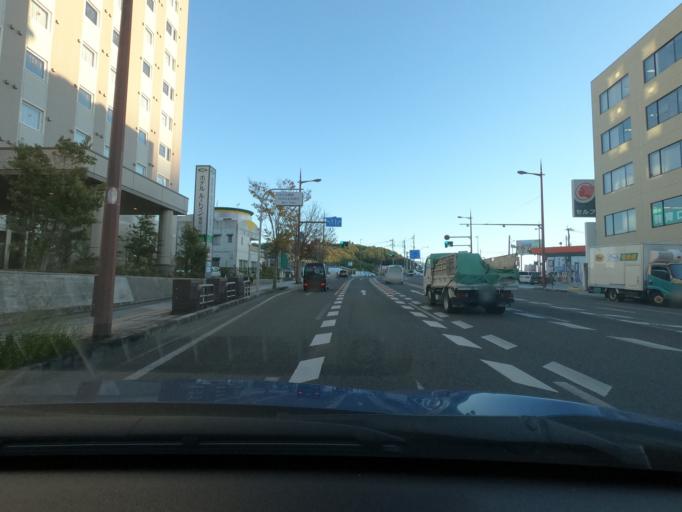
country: JP
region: Kagoshima
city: Satsumasendai
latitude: 31.8130
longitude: 130.3074
